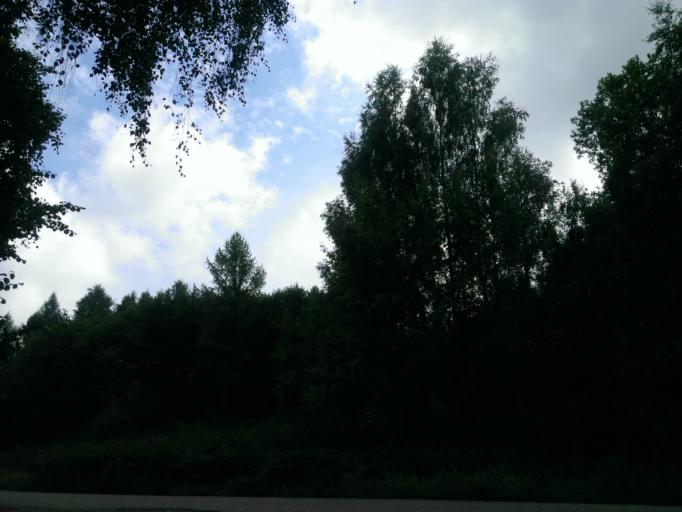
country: LV
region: Amatas Novads
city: Drabesi
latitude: 57.2220
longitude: 25.2232
